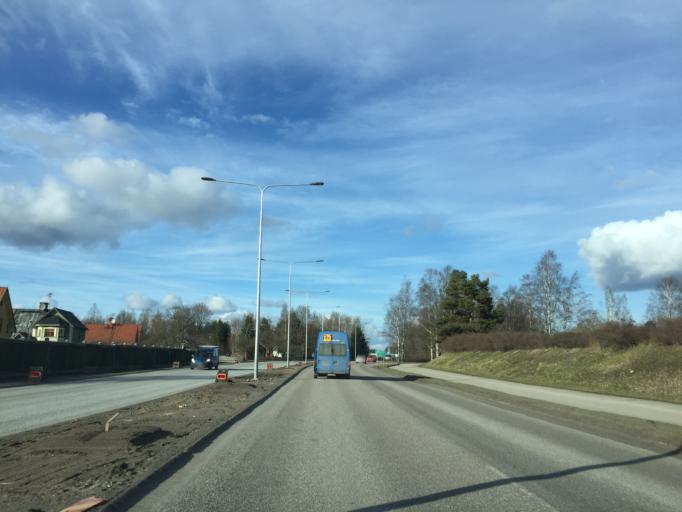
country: SE
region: OErebro
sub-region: Orebro Kommun
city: Orebro
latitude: 59.2920
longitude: 15.2258
